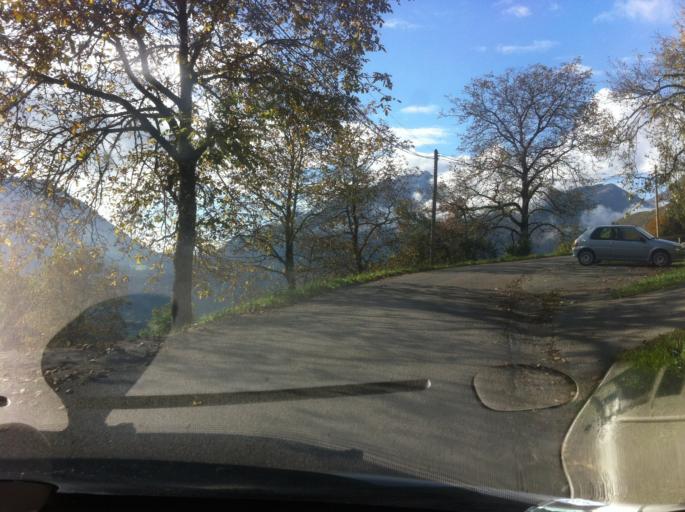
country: FR
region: Rhone-Alpes
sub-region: Departement de la Haute-Savoie
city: Faverges
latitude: 45.7737
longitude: 6.3054
